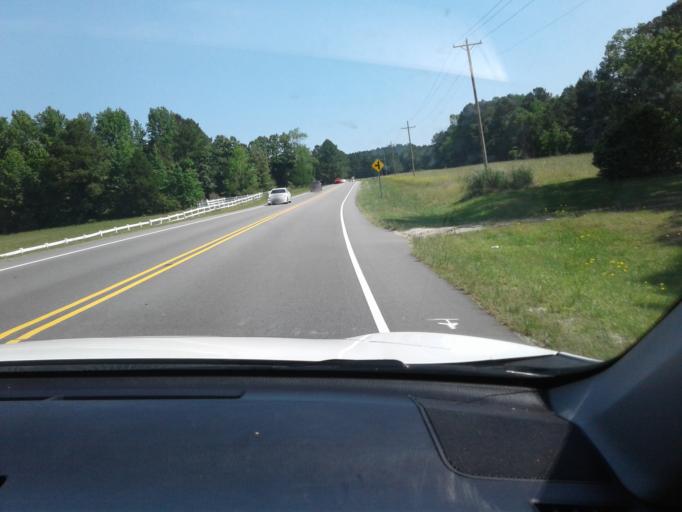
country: US
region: North Carolina
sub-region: Harnett County
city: Lillington
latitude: 35.4369
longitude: -78.8287
